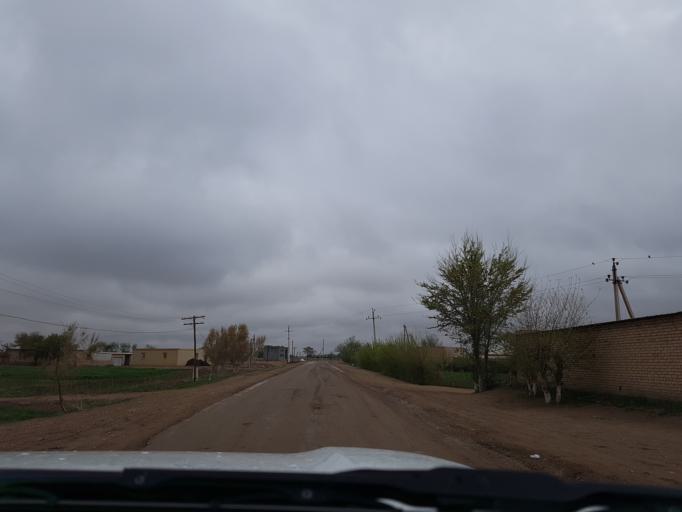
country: TM
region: Lebap
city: Sayat
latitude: 38.4552
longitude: 64.3687
